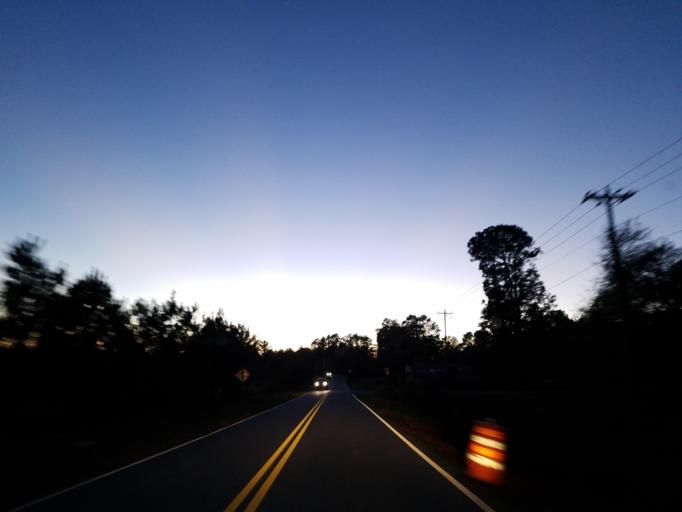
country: US
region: Georgia
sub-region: Dawson County
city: Dawsonville
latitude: 34.3279
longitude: -84.0601
